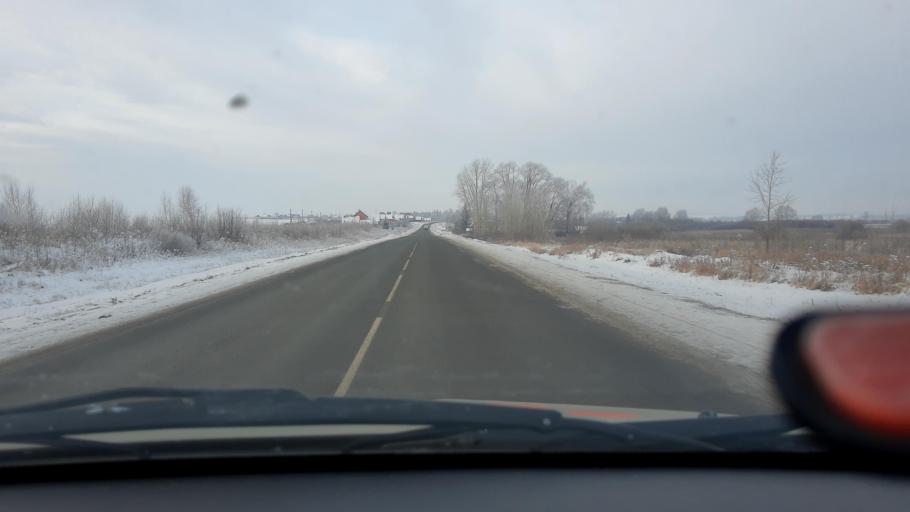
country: RU
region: Bashkortostan
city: Avdon
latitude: 54.3687
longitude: 55.8214
